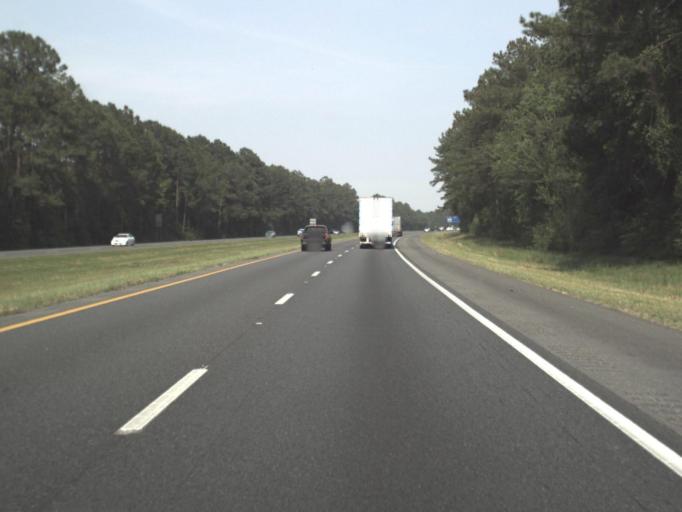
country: US
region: Florida
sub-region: Baker County
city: Macclenny
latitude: 30.2605
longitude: -82.1735
